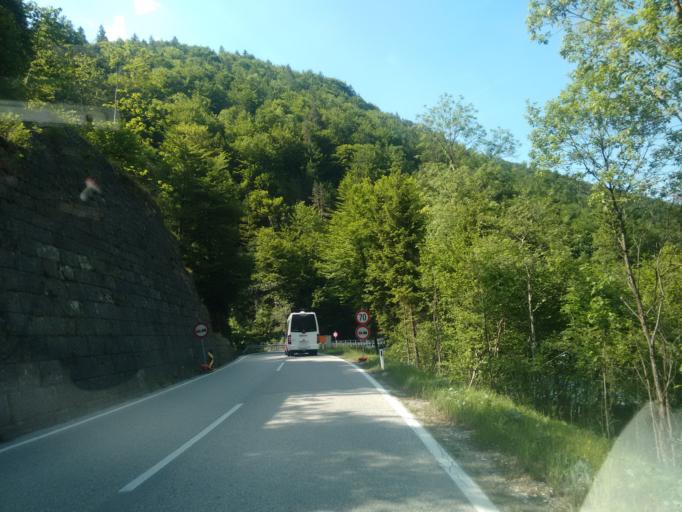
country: AT
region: Upper Austria
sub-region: Politischer Bezirk Kirchdorf an der Krems
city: Rossleithen
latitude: 47.7571
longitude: 14.1637
